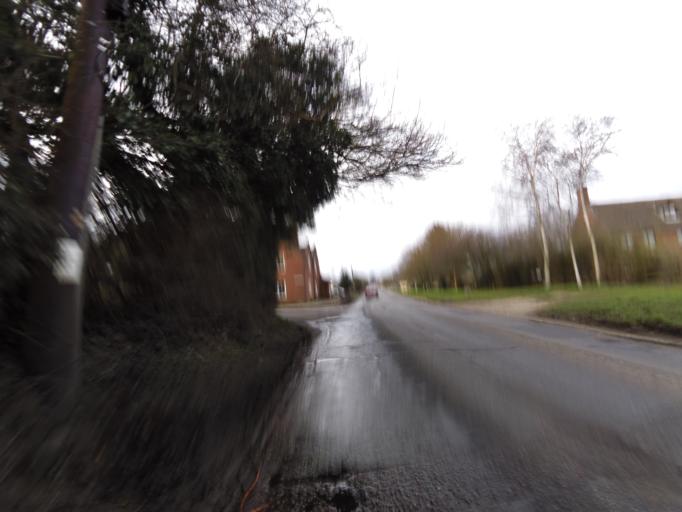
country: GB
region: England
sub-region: Suffolk
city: Ipswich
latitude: 52.0892
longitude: 1.1528
